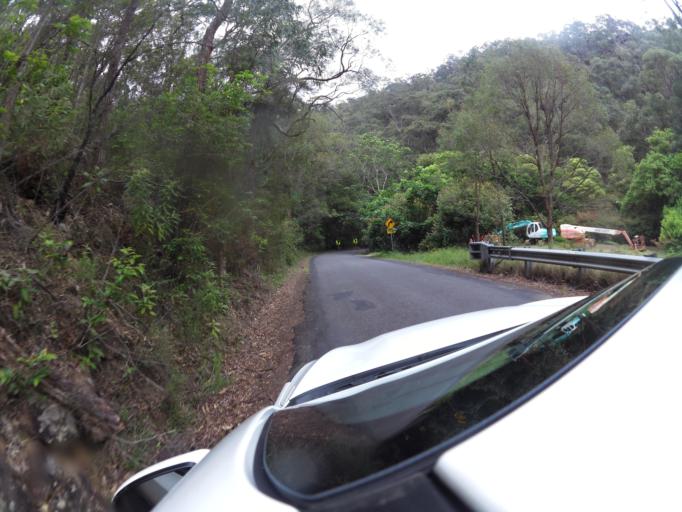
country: AU
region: New South Wales
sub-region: Hornsby Shire
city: Glenorie
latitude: -33.4083
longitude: 150.9714
